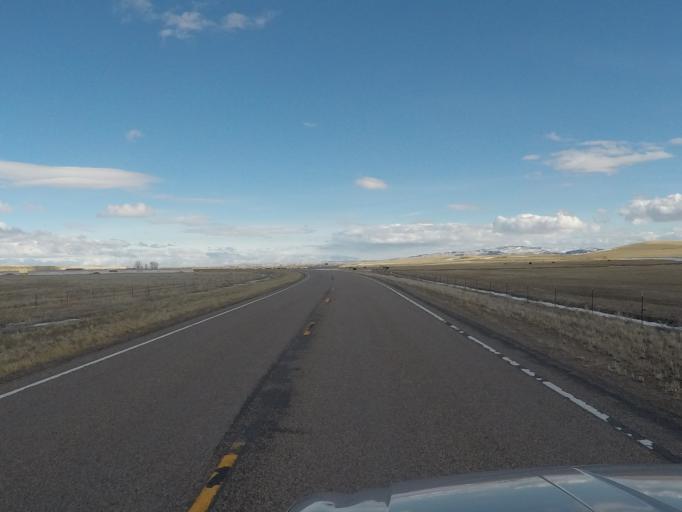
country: US
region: Montana
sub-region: Wheatland County
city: Harlowton
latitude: 46.4899
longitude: -110.3264
